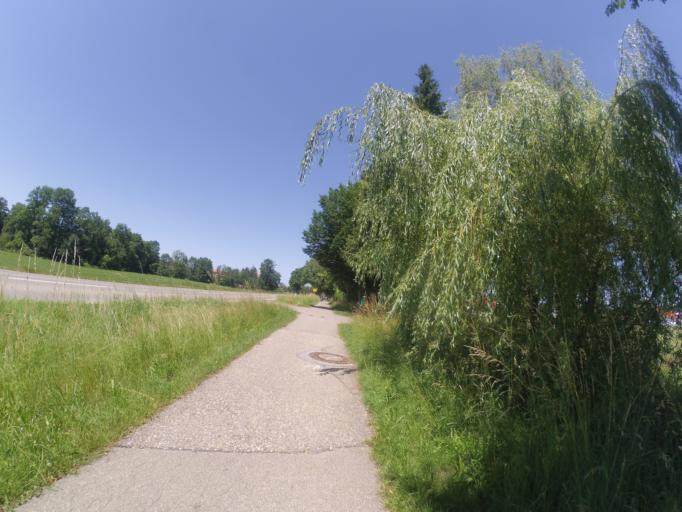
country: DE
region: Bavaria
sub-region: Swabia
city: Ottobeuren
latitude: 47.9328
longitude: 10.3053
